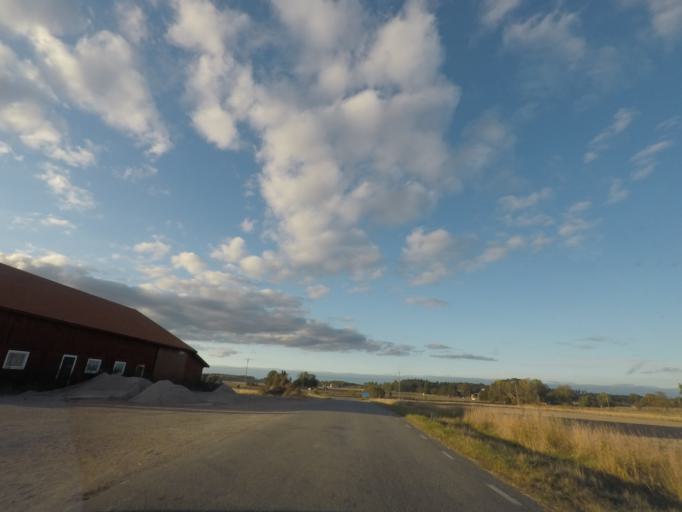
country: SE
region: Vaestmanland
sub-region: Kungsors Kommun
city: Kungsoer
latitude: 59.5271
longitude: 16.1138
